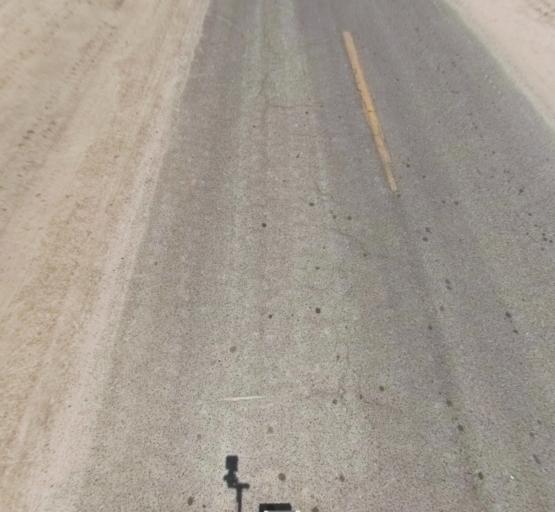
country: US
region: California
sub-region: Fresno County
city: Kerman
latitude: 36.8212
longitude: -120.1509
